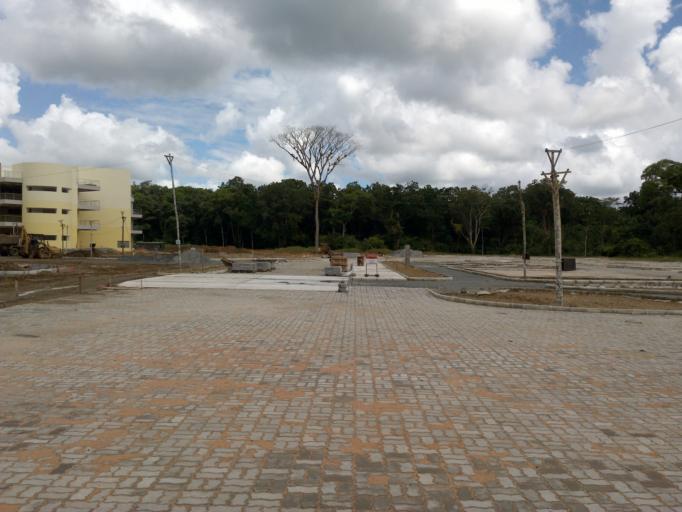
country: BR
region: Bahia
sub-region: Itabuna
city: Itabuna
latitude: -14.7713
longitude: -39.2346
